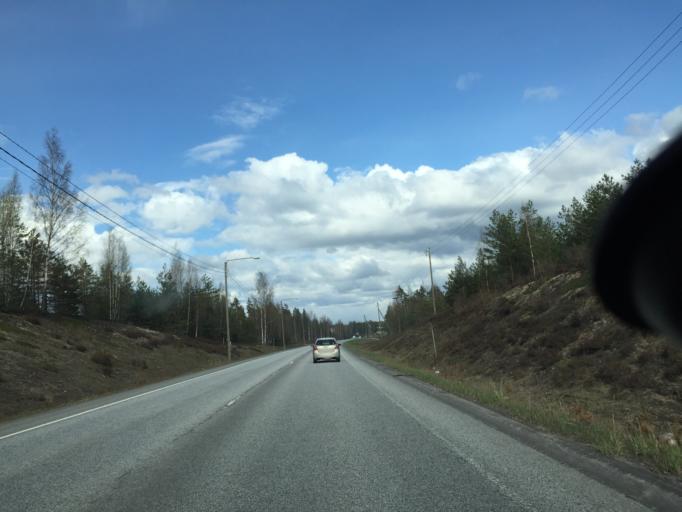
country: FI
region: Uusimaa
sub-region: Raaseporin
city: Pohja
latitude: 60.0121
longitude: 23.5519
